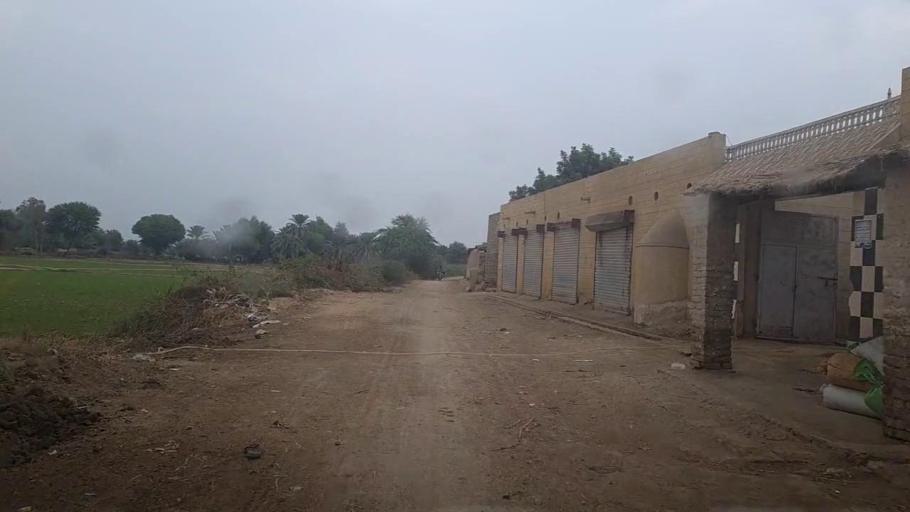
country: PK
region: Sindh
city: Gambat
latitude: 27.3606
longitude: 68.5972
